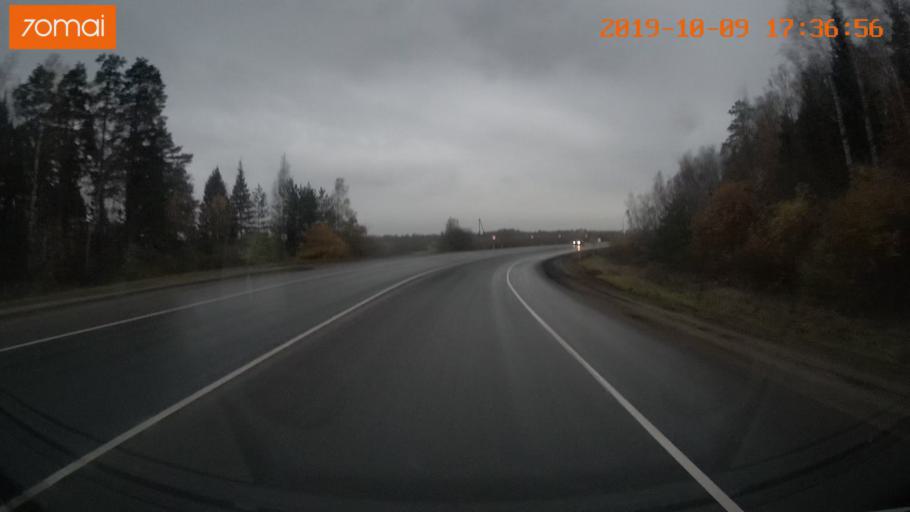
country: RU
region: Ivanovo
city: Bogorodskoye
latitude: 57.0717
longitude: 40.9907
